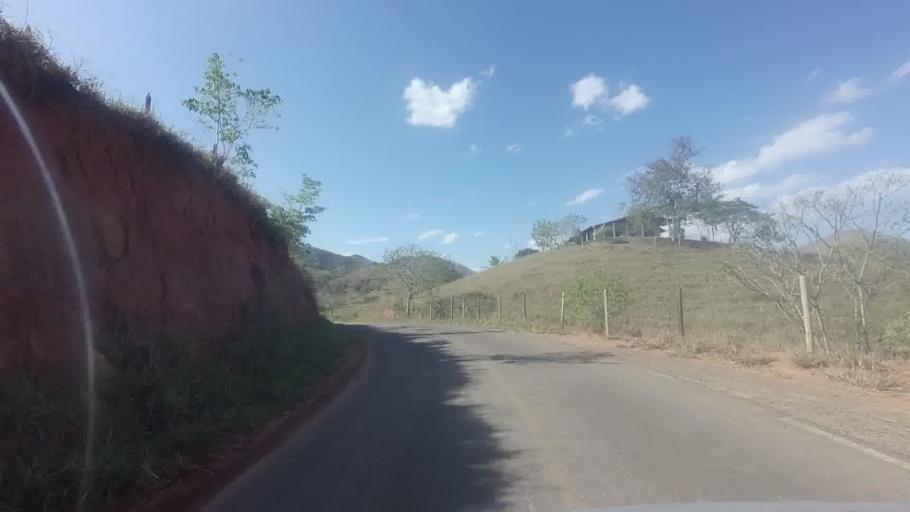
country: BR
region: Rio de Janeiro
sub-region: Bom Jesus Do Itabapoana
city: Bom Jesus do Itabapoana
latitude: -21.1181
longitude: -41.6531
